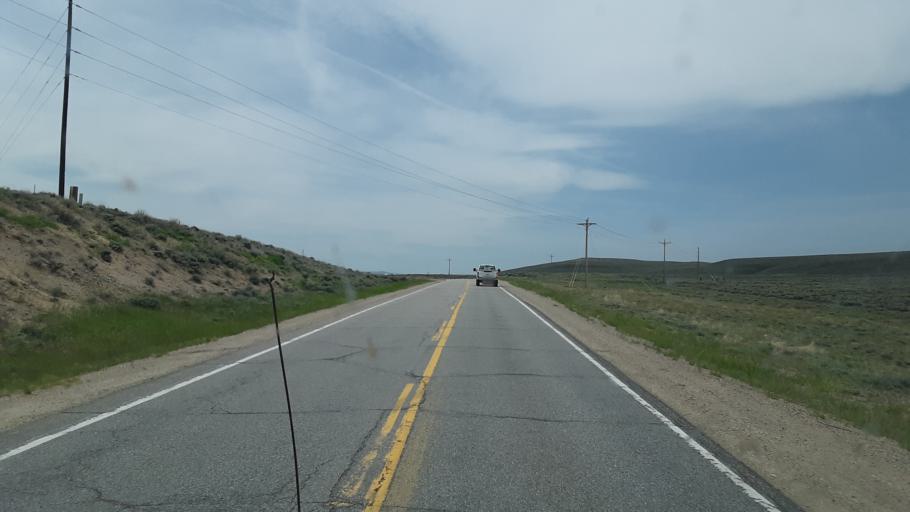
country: US
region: Colorado
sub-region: Jackson County
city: Walden
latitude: 40.6630
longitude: -106.3942
